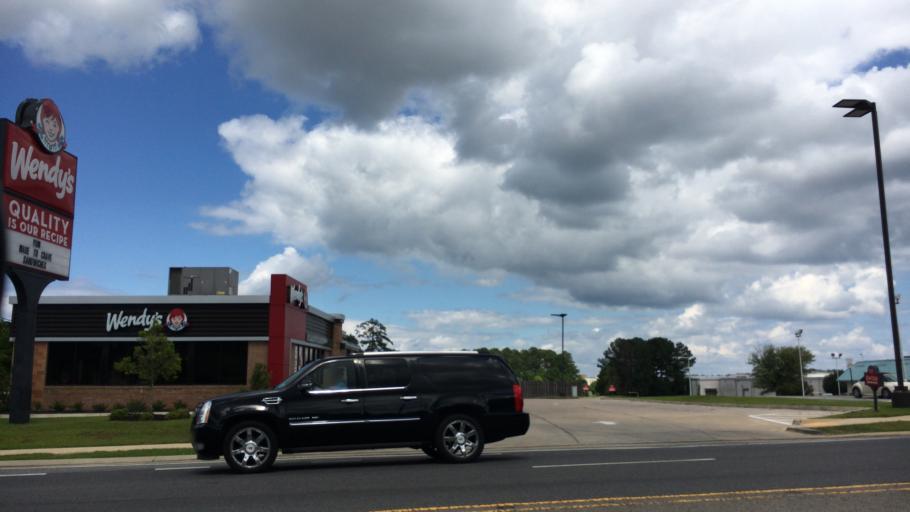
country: US
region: Louisiana
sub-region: Lincoln Parish
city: Ruston
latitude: 32.5436
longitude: -92.6396
